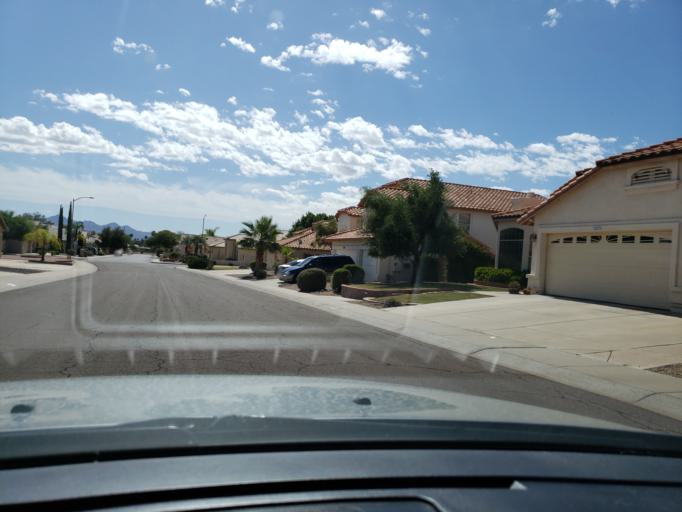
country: US
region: Arizona
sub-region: Maricopa County
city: Paradise Valley
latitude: 33.6148
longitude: -112.0185
